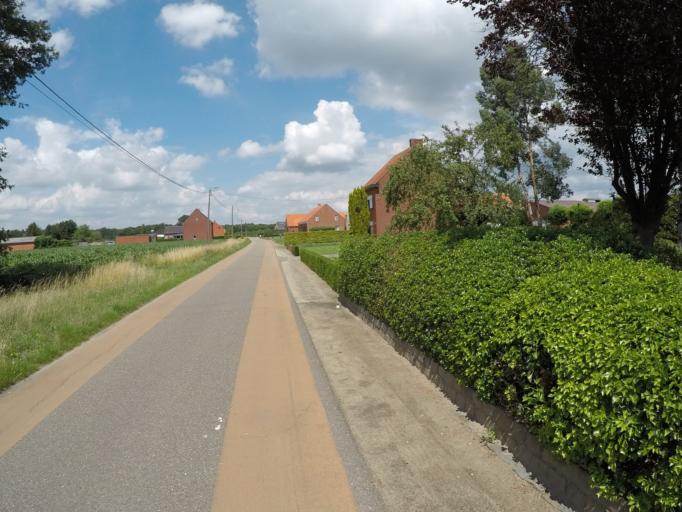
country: BE
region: Flanders
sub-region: Provincie Antwerpen
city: Lille
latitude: 51.2753
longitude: 4.8505
